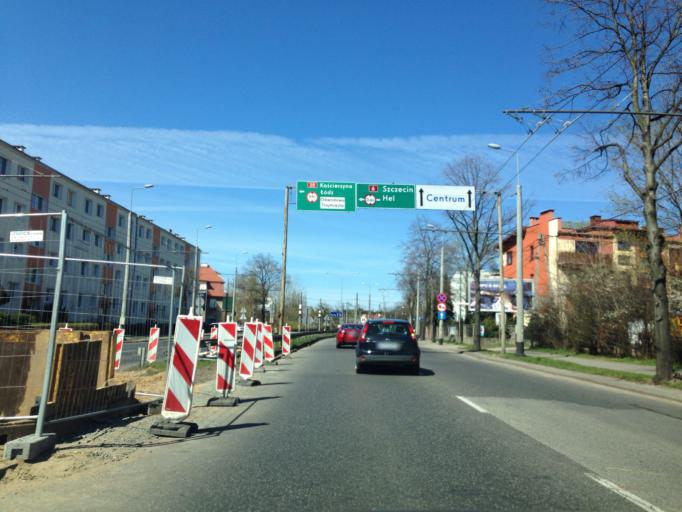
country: PL
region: Pomeranian Voivodeship
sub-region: Gdynia
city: Gdynia
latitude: 54.4830
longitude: 18.5490
